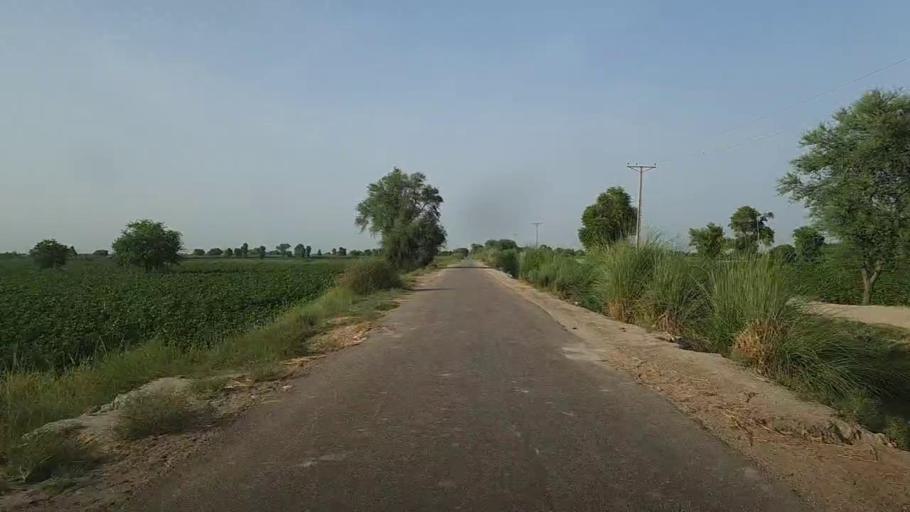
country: PK
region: Sindh
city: Ubauro
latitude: 28.0908
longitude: 69.8193
